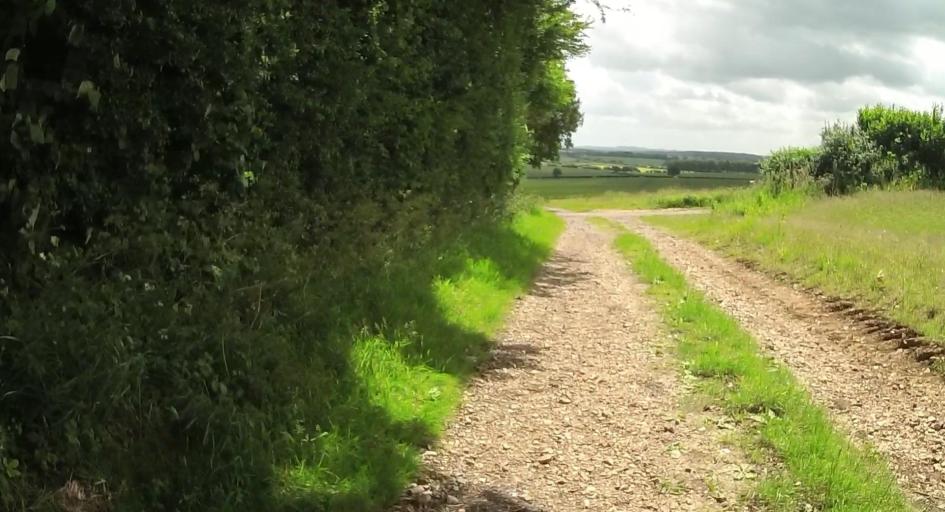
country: GB
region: England
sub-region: Hampshire
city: Basingstoke
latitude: 51.1784
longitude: -1.1651
